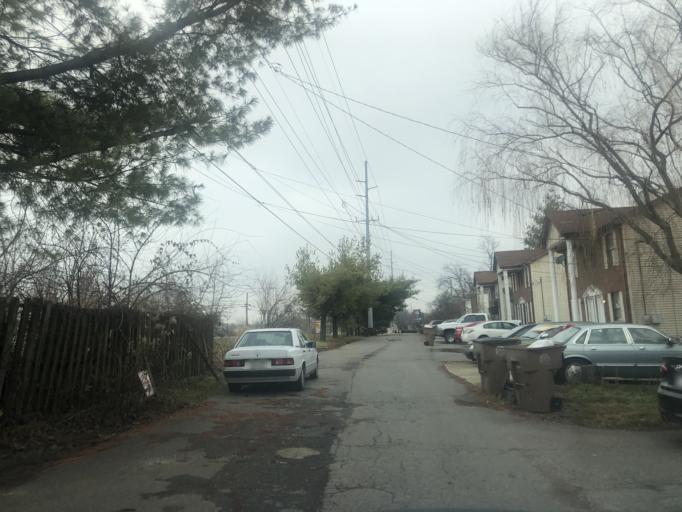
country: US
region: Tennessee
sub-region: Rutherford County
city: La Vergne
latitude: 36.0816
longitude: -86.6461
